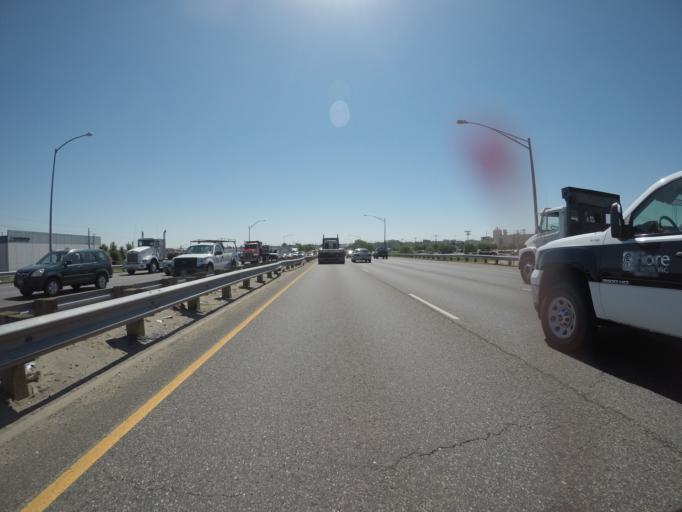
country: US
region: Colorado
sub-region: Adams County
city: Commerce City
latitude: 39.7797
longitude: -104.9306
